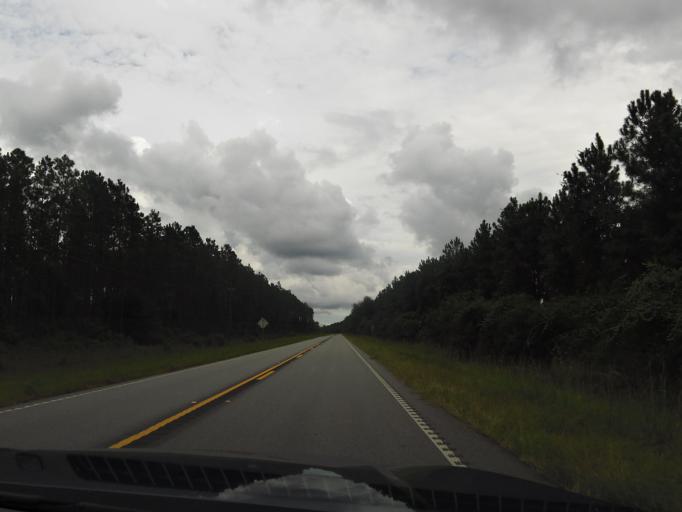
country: US
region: Florida
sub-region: Baker County
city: Macclenny
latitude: 30.5221
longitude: -82.1982
